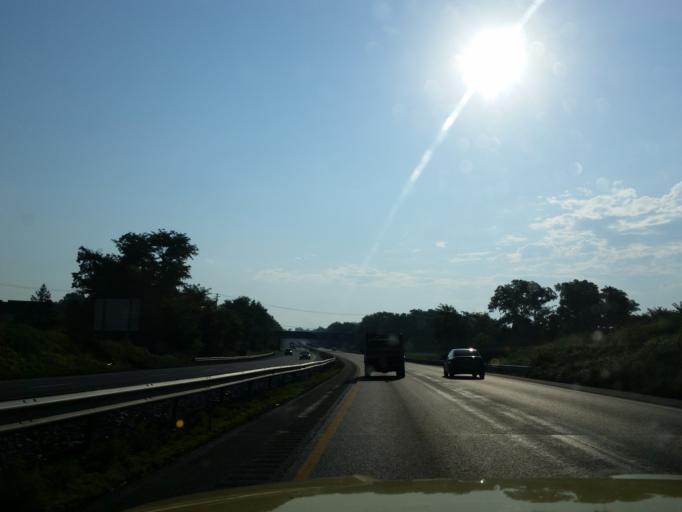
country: US
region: Pennsylvania
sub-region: Lancaster County
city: Mountville
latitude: 40.0413
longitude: -76.4401
